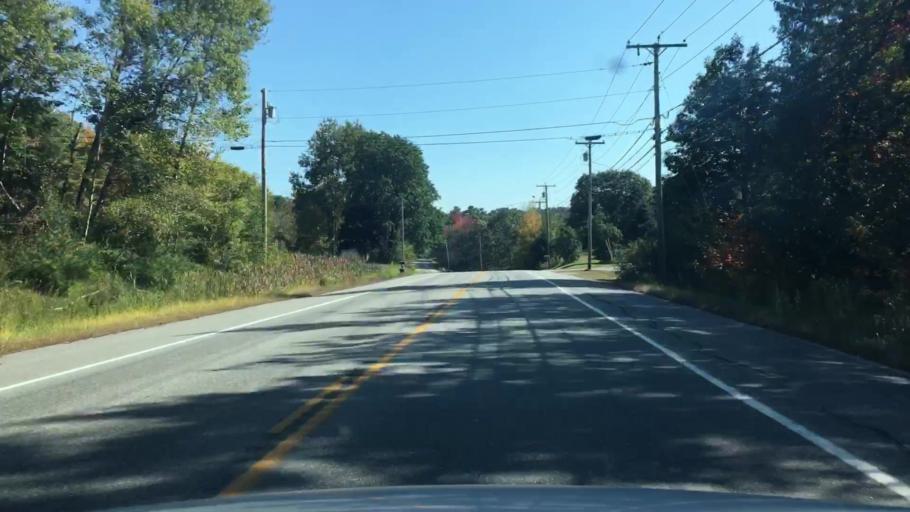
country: US
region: Maine
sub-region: Androscoggin County
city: Lisbon Falls
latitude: 43.9861
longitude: -70.0402
